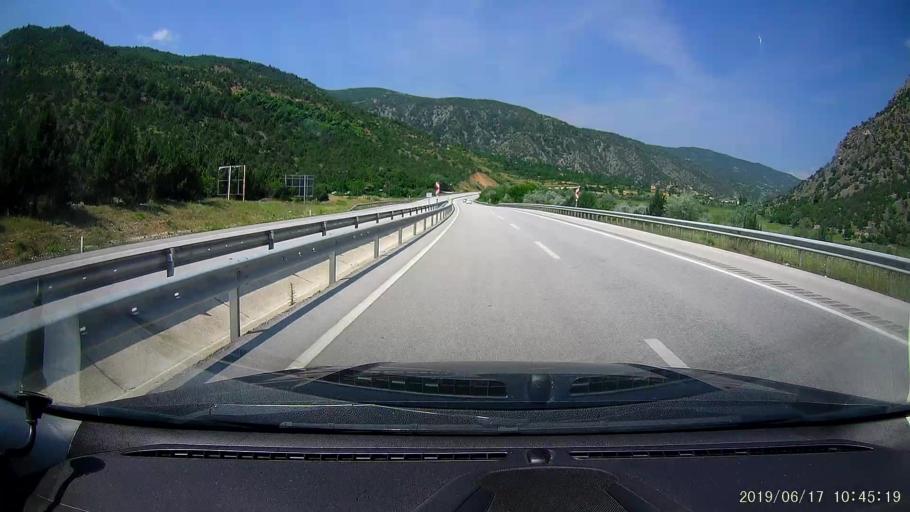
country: TR
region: Corum
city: Hacihamza
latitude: 41.0639
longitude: 34.4918
